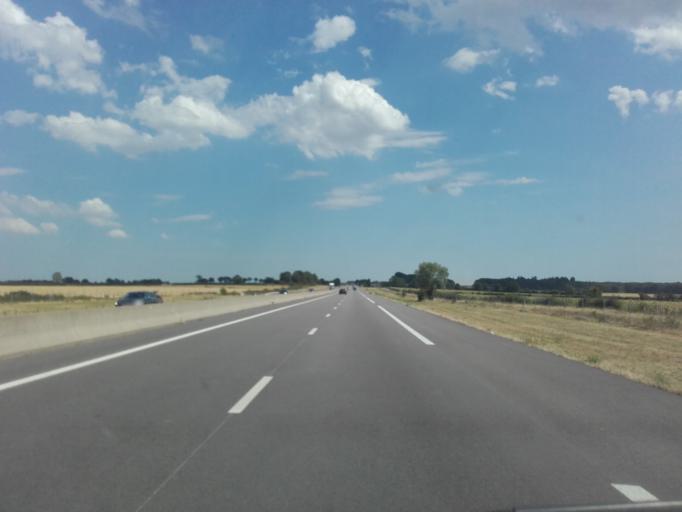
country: FR
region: Bourgogne
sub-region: Departement de la Cote-d'Or
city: Semur-en-Auxois
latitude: 47.4808
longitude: 4.1819
